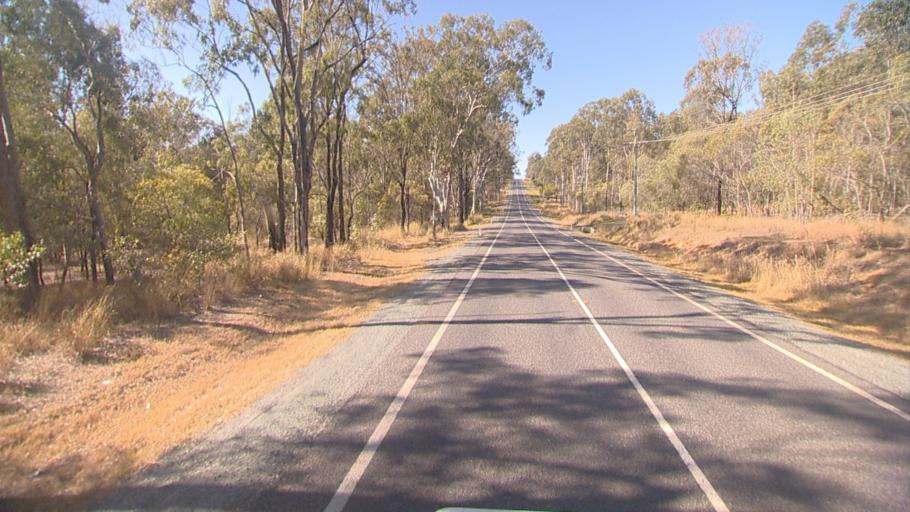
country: AU
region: Queensland
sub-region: Logan
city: Cedar Vale
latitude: -27.8521
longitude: 153.0261
